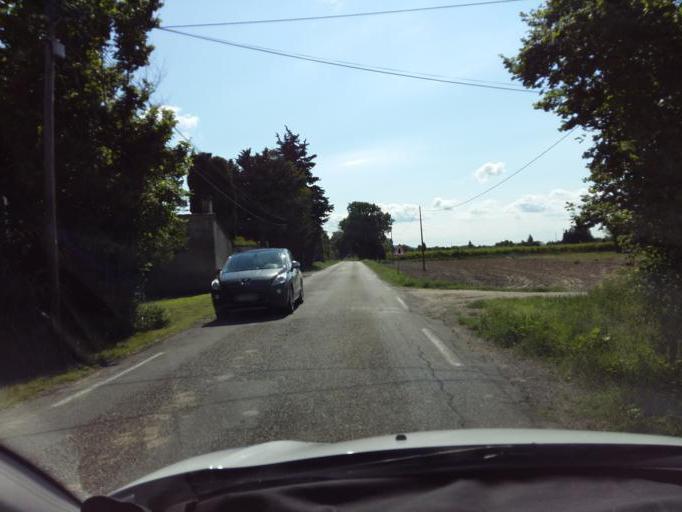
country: FR
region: Provence-Alpes-Cote d'Azur
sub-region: Departement du Vaucluse
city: Robion
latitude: 43.8621
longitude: 5.1024
